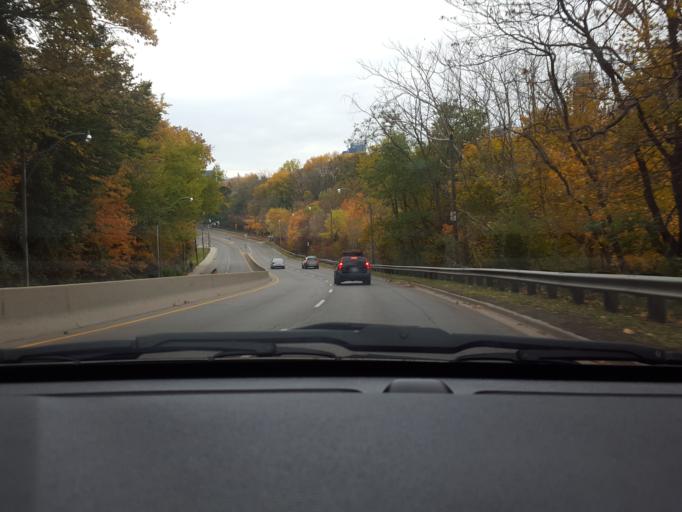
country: CA
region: Ontario
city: Toronto
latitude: 43.6827
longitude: -79.3834
